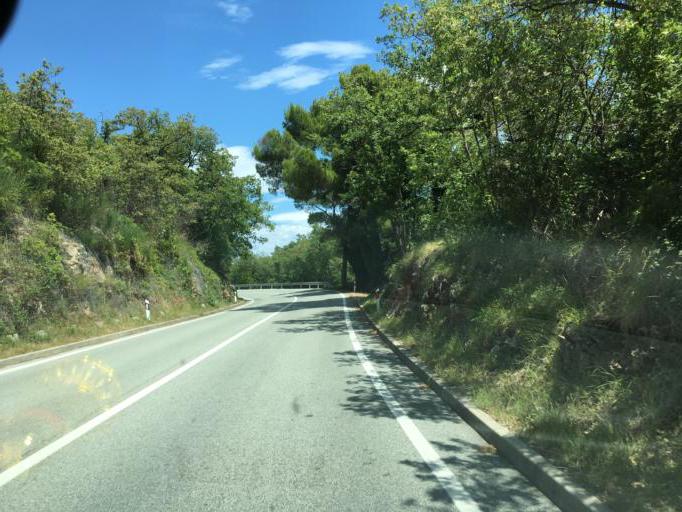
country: HR
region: Istarska
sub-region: Grad Labin
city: Rabac
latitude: 45.1315
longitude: 14.2046
